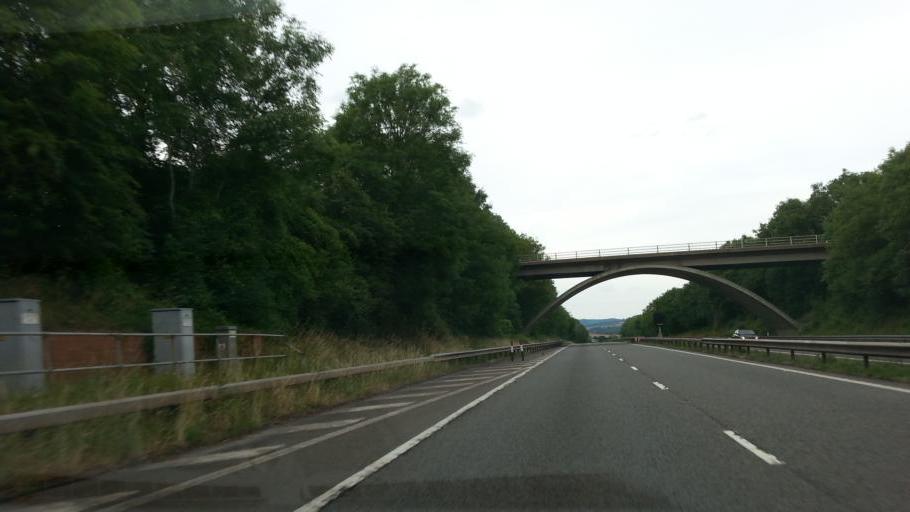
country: GB
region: England
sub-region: Herefordshire
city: Donnington
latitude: 51.9658
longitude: -2.4265
